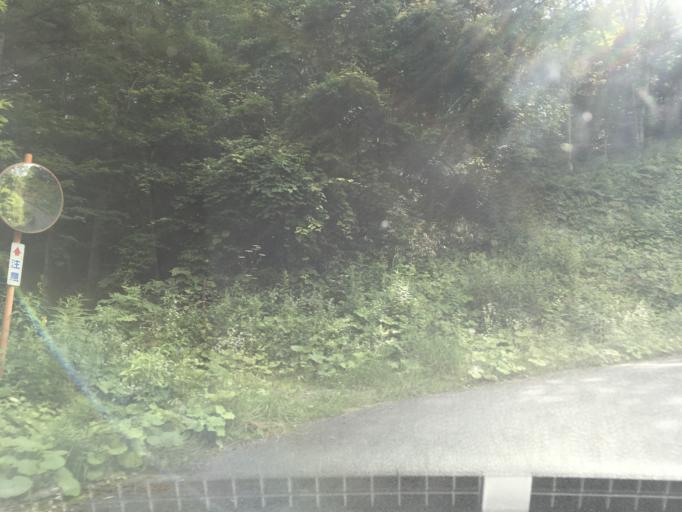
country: JP
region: Iwate
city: Ofunato
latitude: 38.9783
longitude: 141.4527
